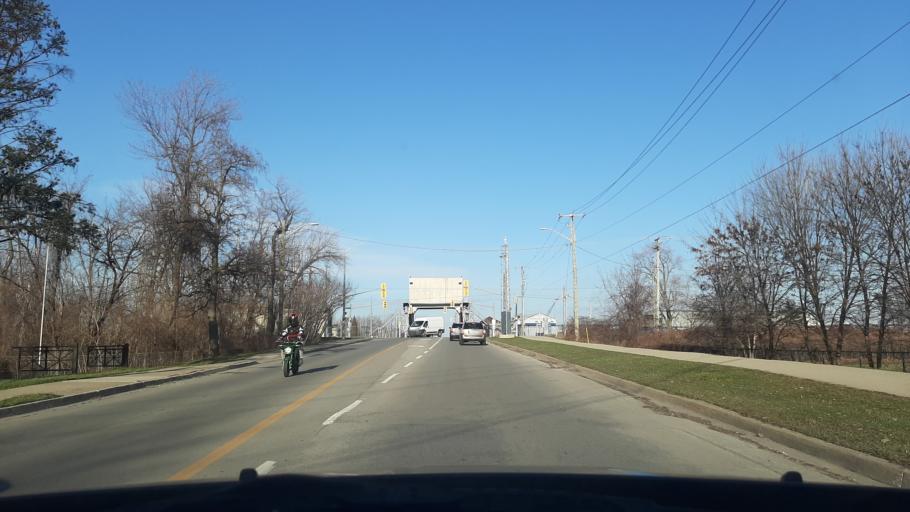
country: CA
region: Ontario
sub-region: Regional Municipality of Niagara
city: St. Catharines
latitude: 43.2153
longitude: -79.2150
